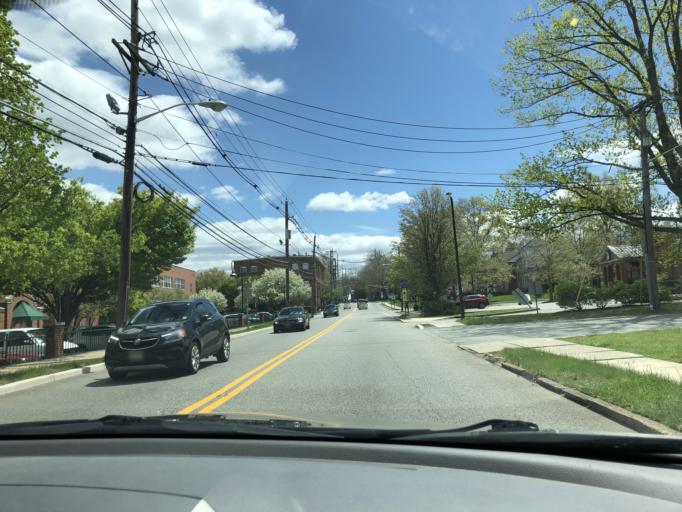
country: US
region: New Jersey
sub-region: Passaic County
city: Singac
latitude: 40.8836
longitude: -74.2356
